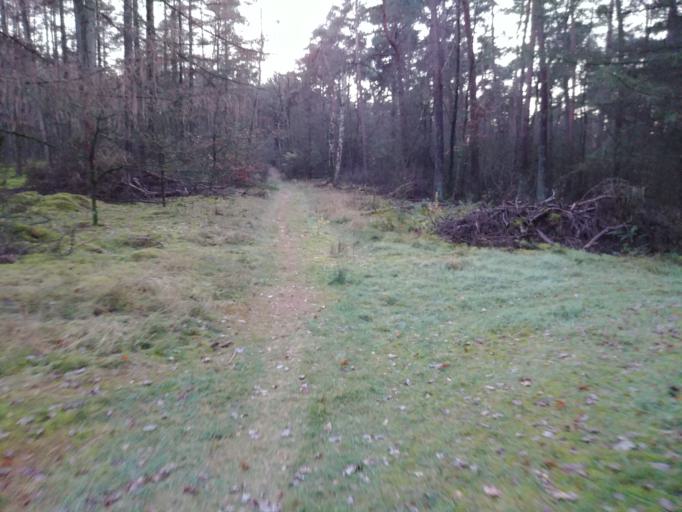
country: NL
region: Utrecht
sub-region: Gemeente Utrechtse Heuvelrug
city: Maarn
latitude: 52.0462
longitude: 5.3813
